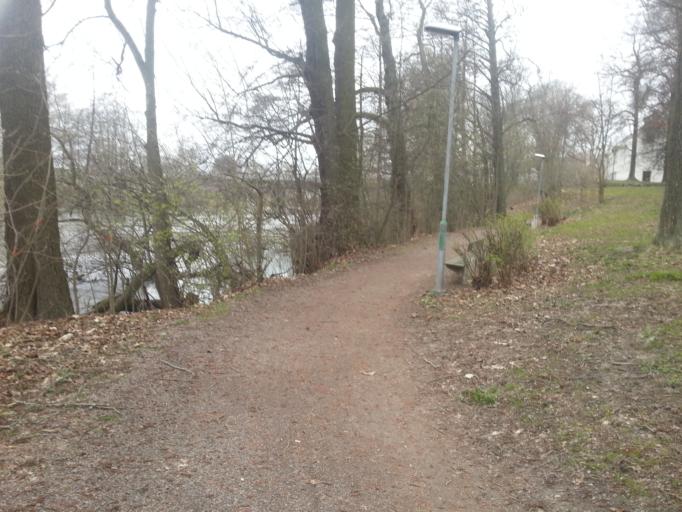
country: SE
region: OEstergoetland
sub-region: Norrkopings Kommun
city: Norrkoping
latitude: 58.5872
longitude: 16.1541
